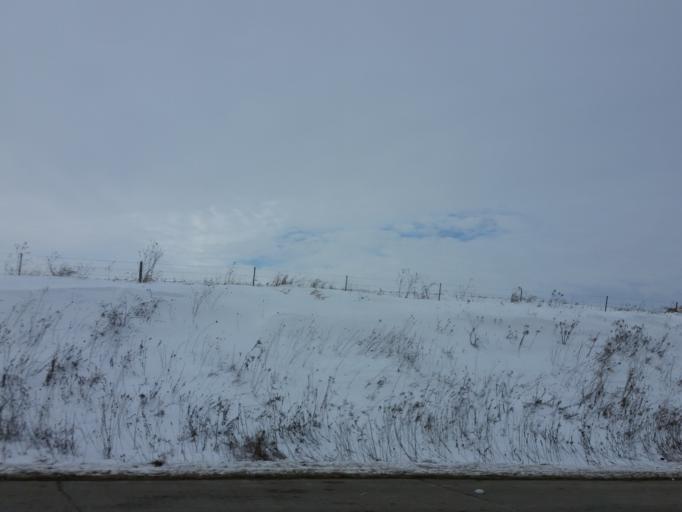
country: US
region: Iowa
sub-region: Dubuque County
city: Peosta
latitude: 42.4057
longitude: -90.8502
